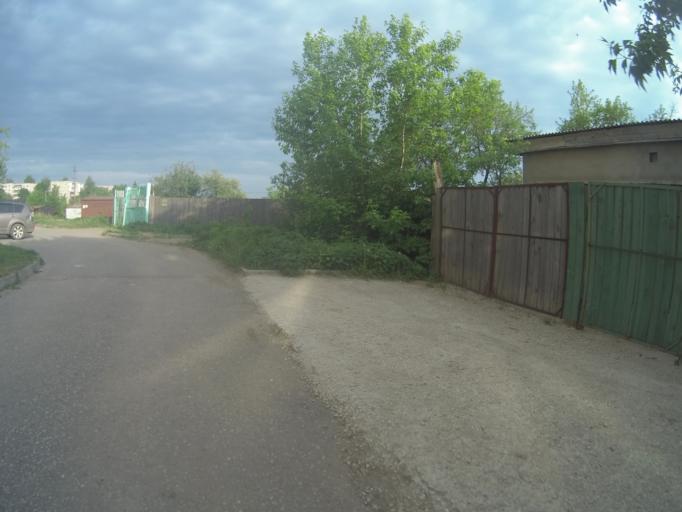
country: RU
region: Vladimir
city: Kommunar
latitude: 56.1599
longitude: 40.4523
